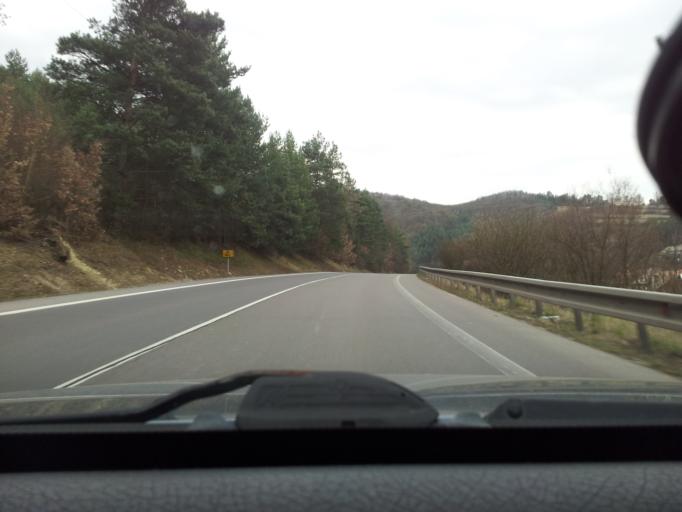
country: SK
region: Banskobystricky
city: Ziar nad Hronom
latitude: 48.6037
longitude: 18.8917
